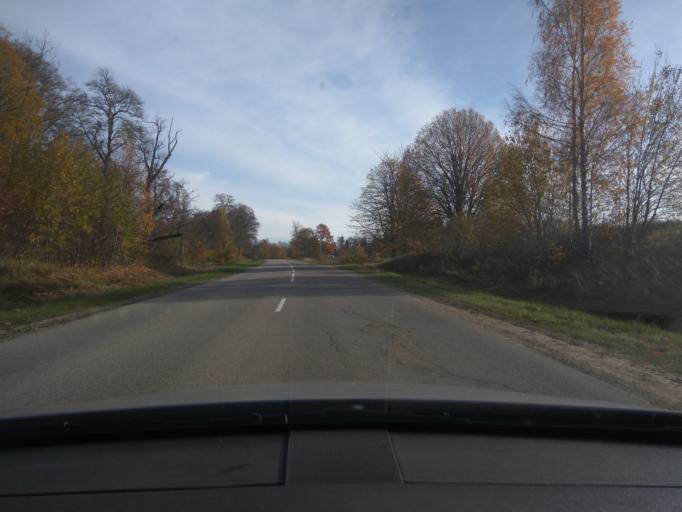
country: LV
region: Alsunga
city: Alsunga
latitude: 57.0140
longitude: 21.7015
